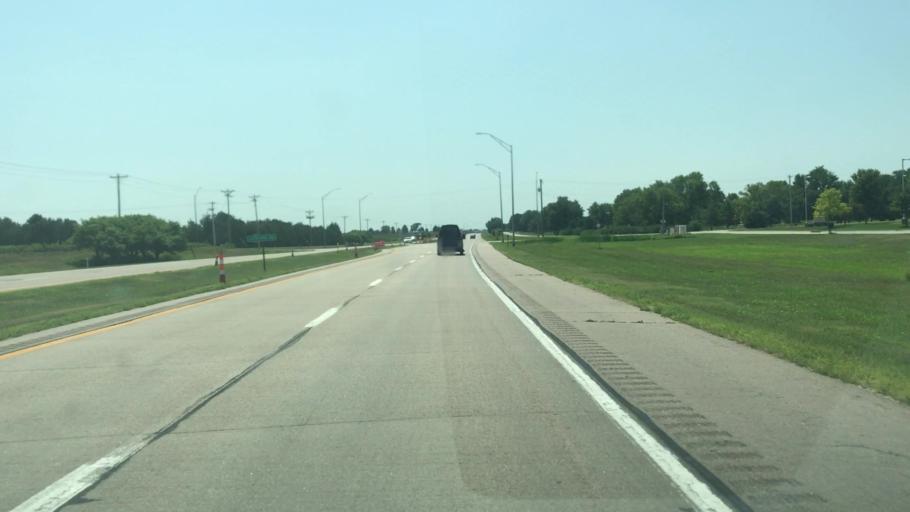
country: US
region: Nebraska
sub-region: Adams County
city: Hastings
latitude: 40.6422
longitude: -98.3820
